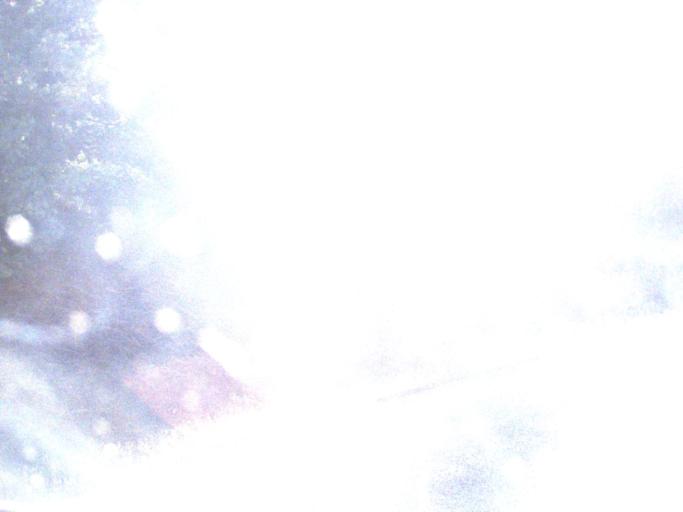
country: CA
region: British Columbia
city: Rossland
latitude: 48.8989
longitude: -117.8062
